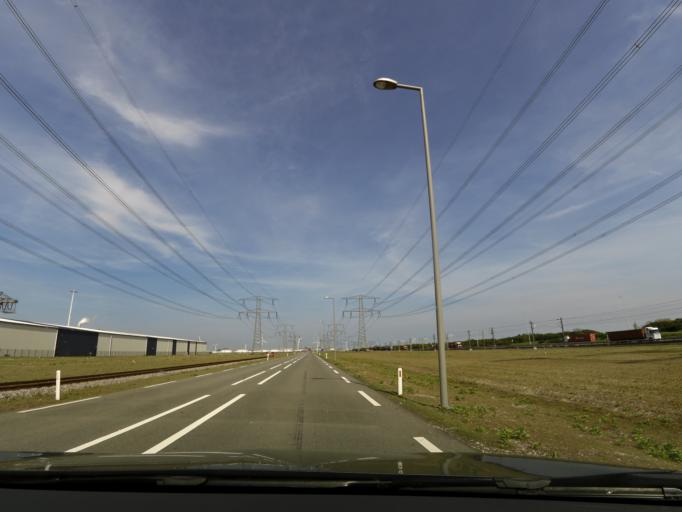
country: NL
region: South Holland
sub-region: Gemeente Rotterdam
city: Hoek van Holland
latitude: 51.9317
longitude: 4.0562
